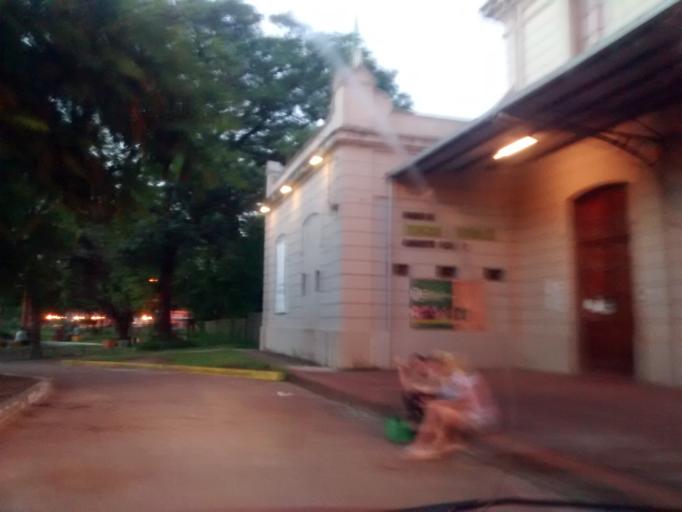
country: AR
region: Chaco
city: Resistencia
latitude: -27.4462
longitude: -58.9774
